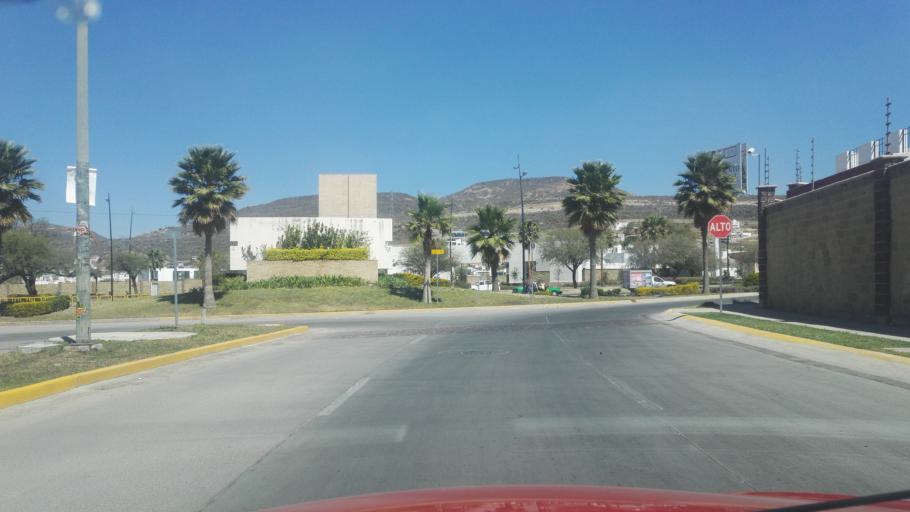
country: MX
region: Guanajuato
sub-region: Leon
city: Medina
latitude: 21.1299
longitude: -101.6054
